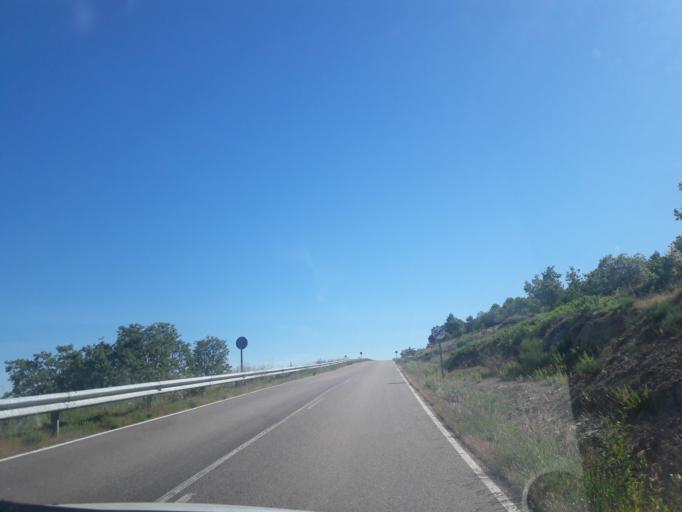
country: ES
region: Castille and Leon
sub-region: Provincia de Salamanca
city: Montemayor del Rio
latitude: 40.3227
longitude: -5.9232
